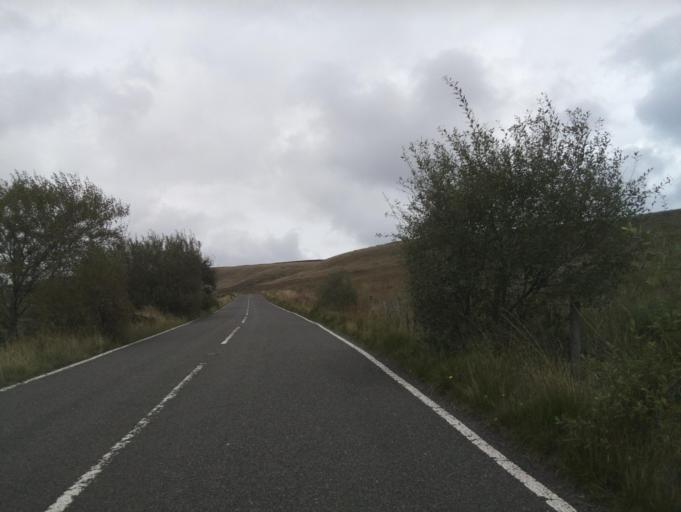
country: GB
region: England
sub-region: Kirklees
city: Meltham
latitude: 53.5174
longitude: -1.8516
